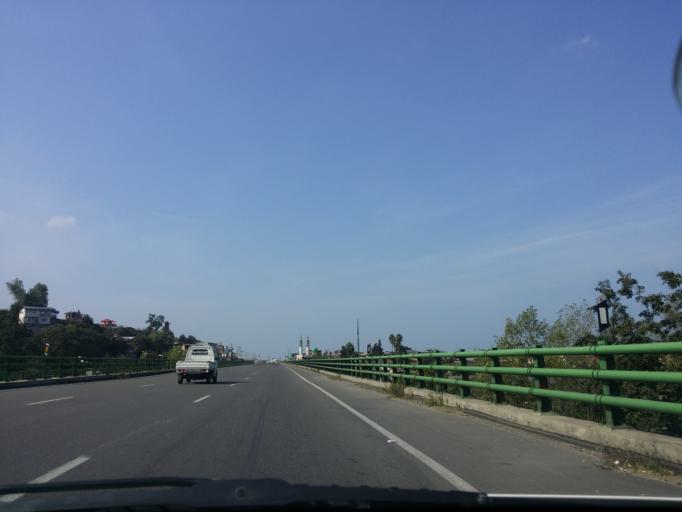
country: IR
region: Mazandaran
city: Chalus
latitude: 36.6470
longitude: 51.4127
